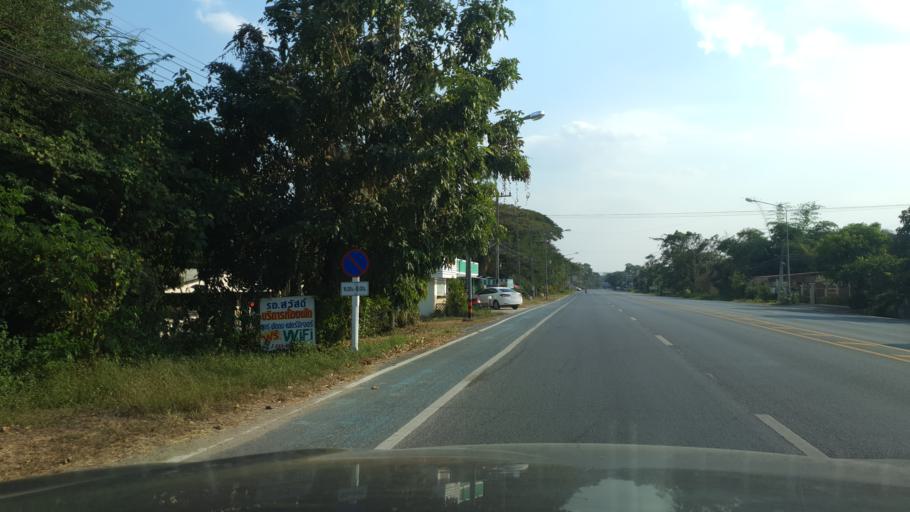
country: TH
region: Tak
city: Tak
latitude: 16.8641
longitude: 99.1204
